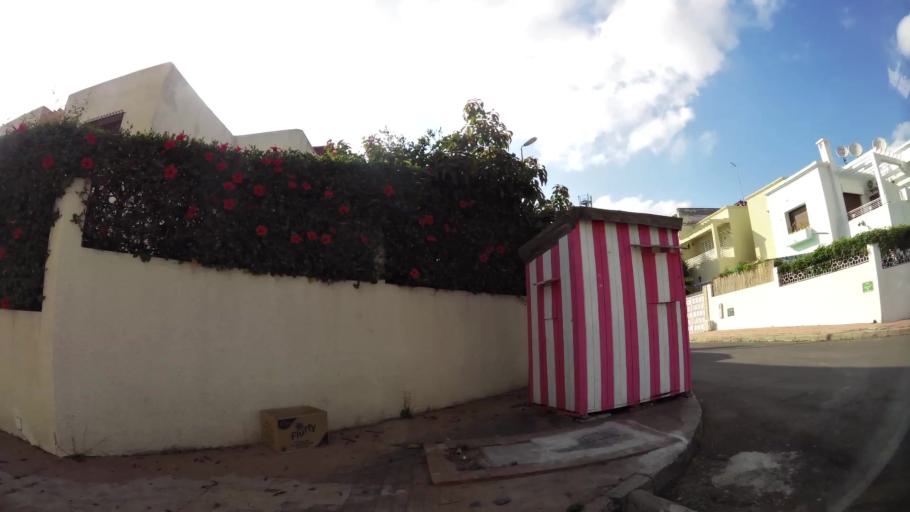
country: MA
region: Rabat-Sale-Zemmour-Zaer
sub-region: Skhirate-Temara
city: Temara
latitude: 33.9544
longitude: -6.8614
